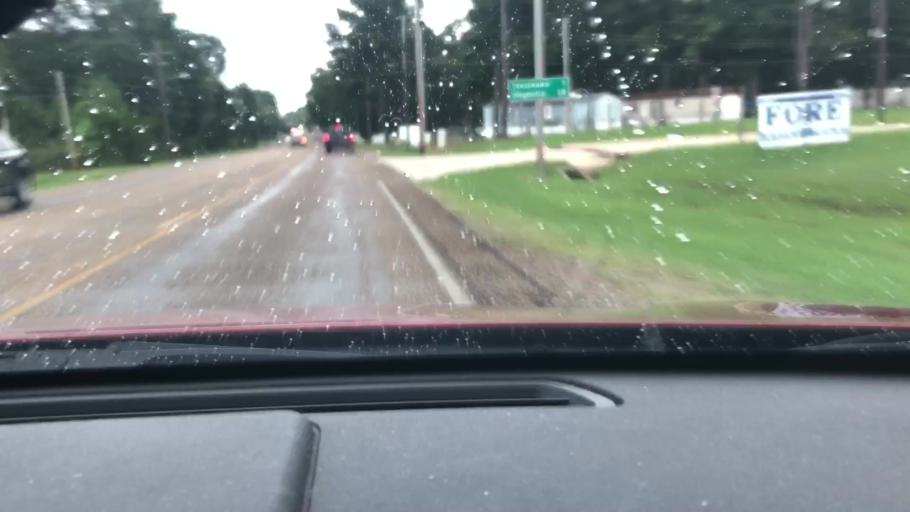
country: US
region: Texas
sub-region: Bowie County
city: Nash
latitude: 33.4426
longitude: -94.1188
